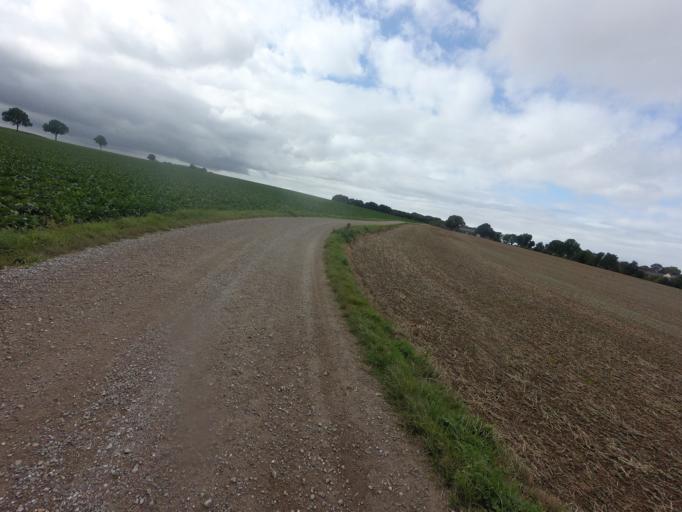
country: NL
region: Limburg
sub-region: Eijsden-Margraten
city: Margraten
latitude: 50.8102
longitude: 5.8387
